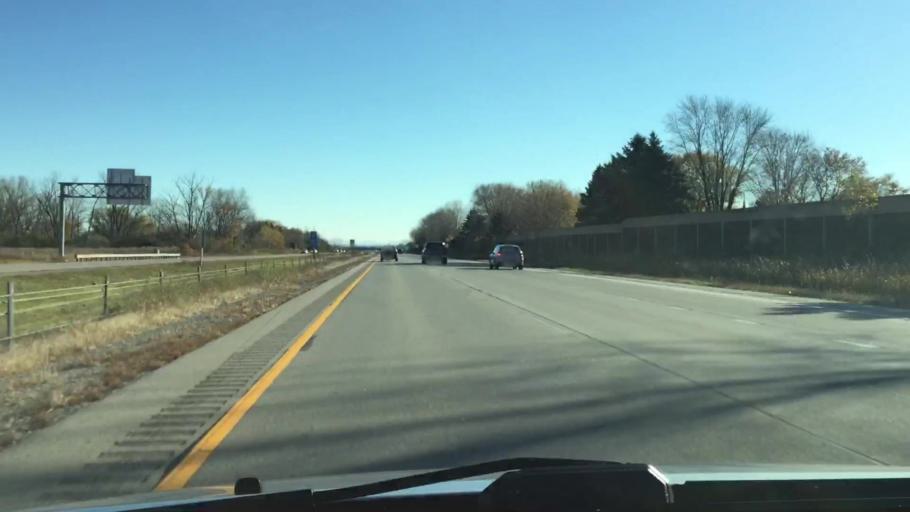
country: US
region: Wisconsin
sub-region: Outagamie County
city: Appleton
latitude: 44.2983
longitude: -88.4097
